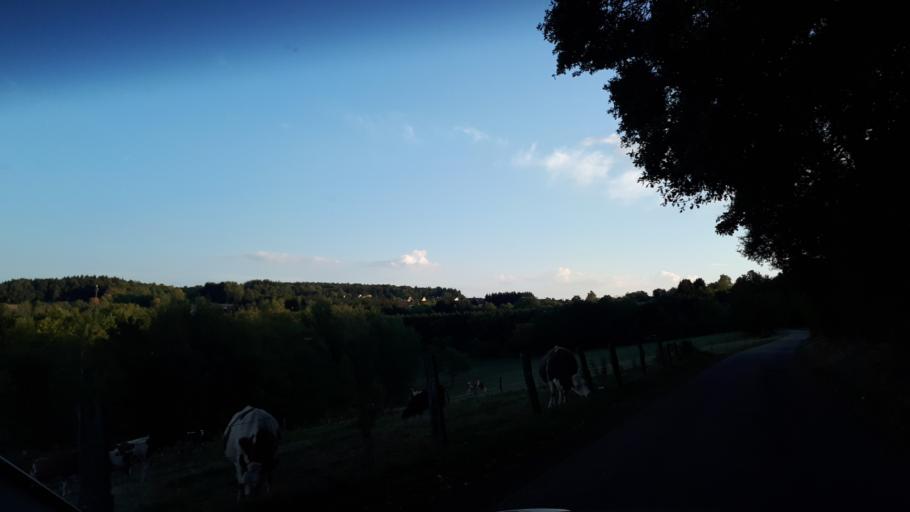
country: DE
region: Saarland
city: Eppelborn
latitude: 49.4000
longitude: 7.0075
